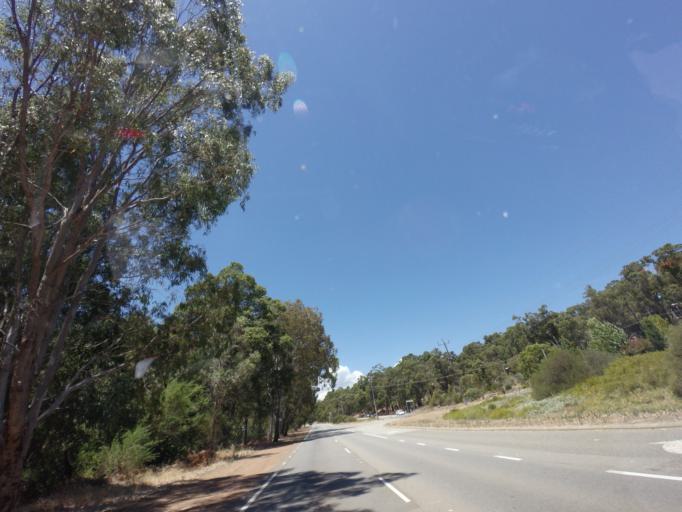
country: AU
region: Western Australia
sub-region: Mundaring
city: Parkerville
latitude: -31.8999
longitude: 116.1349
